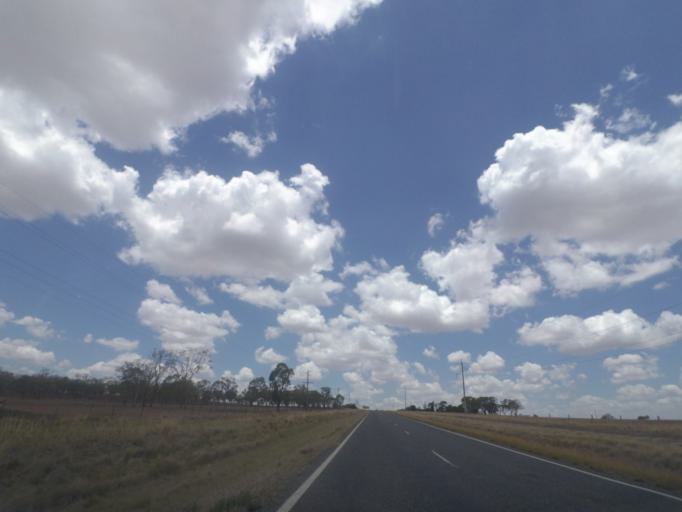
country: AU
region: Queensland
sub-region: Toowoomba
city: Top Camp
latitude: -27.8807
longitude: 151.9697
